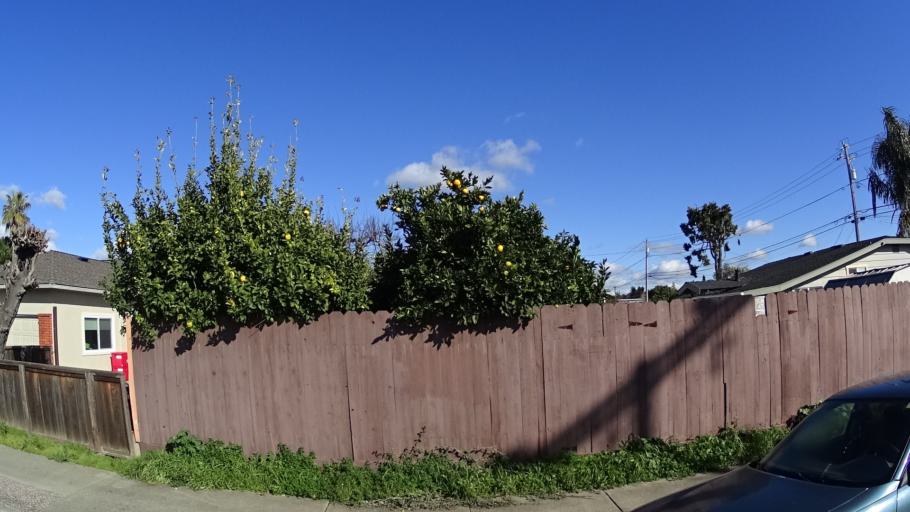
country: US
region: California
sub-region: Alameda County
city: Cherryland
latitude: 37.6813
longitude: -122.1084
